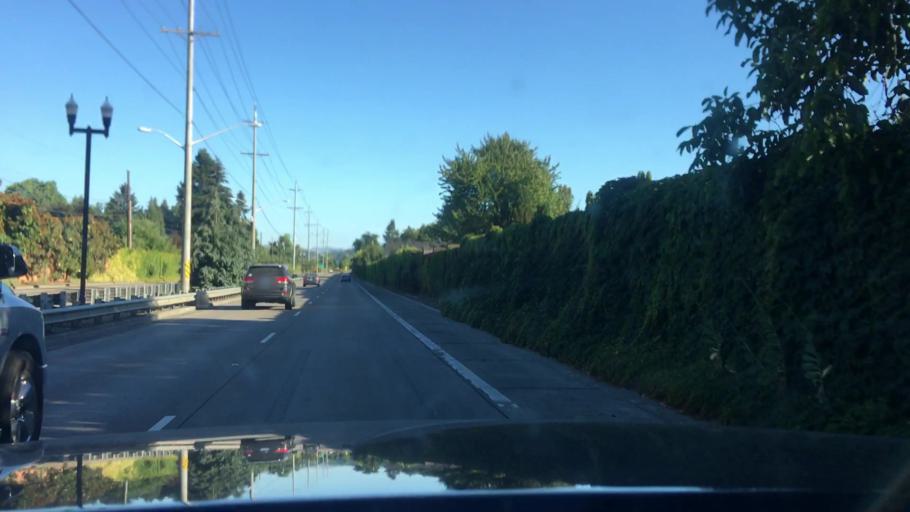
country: US
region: Oregon
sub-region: Lane County
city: Springfield
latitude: 44.0762
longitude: -123.0309
